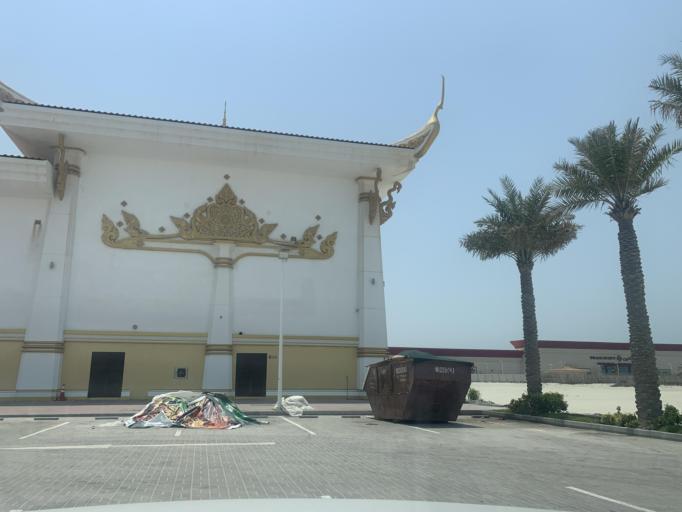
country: BH
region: Muharraq
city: Al Muharraq
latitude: 26.3067
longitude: 50.6273
